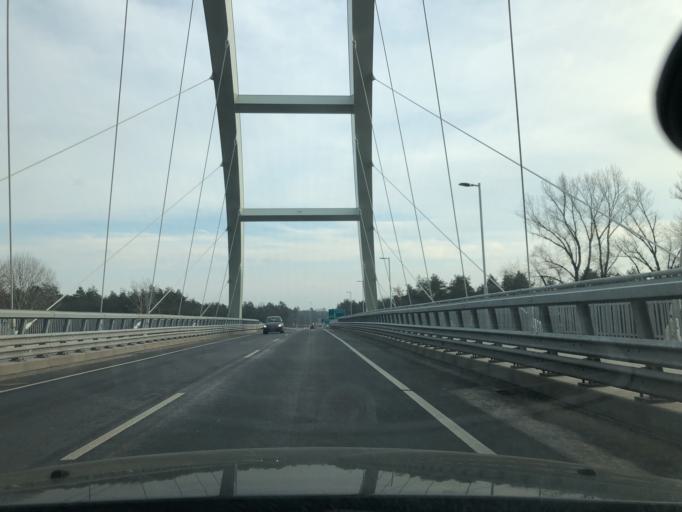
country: HU
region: Gyor-Moson-Sopron
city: Gyor
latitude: 47.7272
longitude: 17.7016
